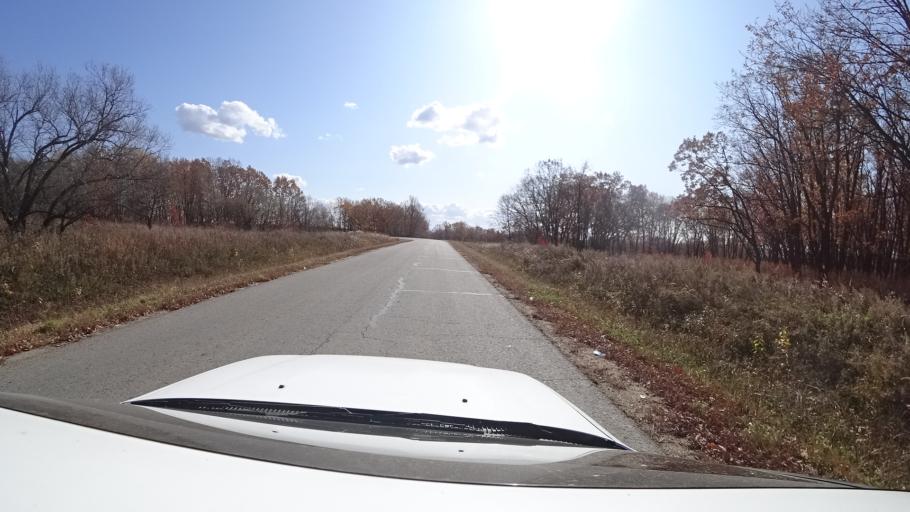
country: RU
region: Primorskiy
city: Lazo
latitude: 45.8689
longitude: 133.6614
